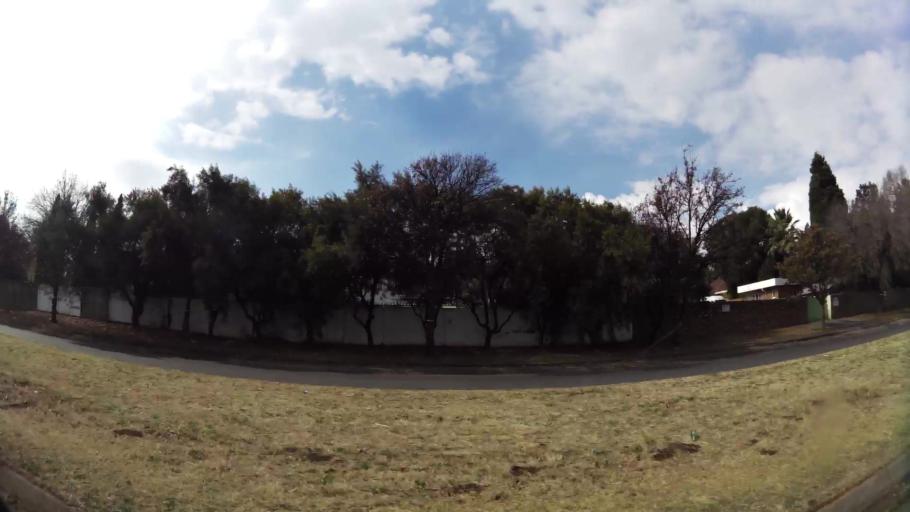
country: ZA
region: Gauteng
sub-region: Sedibeng District Municipality
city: Vanderbijlpark
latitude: -26.7381
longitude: 27.8437
